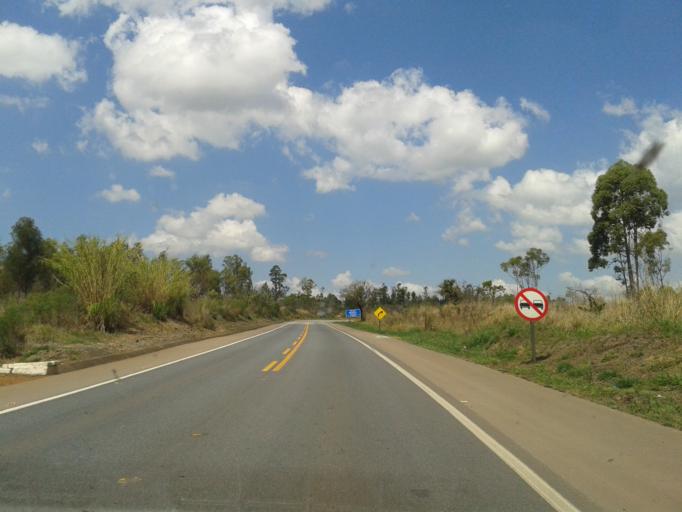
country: BR
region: Minas Gerais
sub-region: Campos Altos
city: Campos Altos
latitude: -19.6713
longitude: -46.0463
